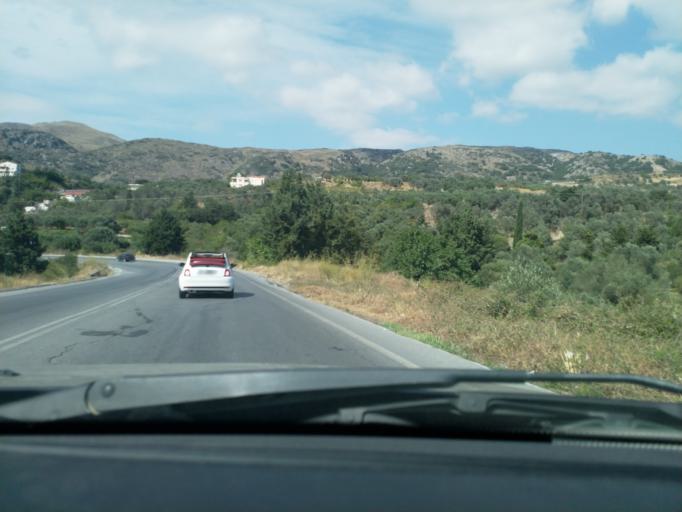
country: GR
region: Crete
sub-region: Nomos Rethymnis
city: Agia Foteini
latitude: 35.2202
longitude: 24.5005
